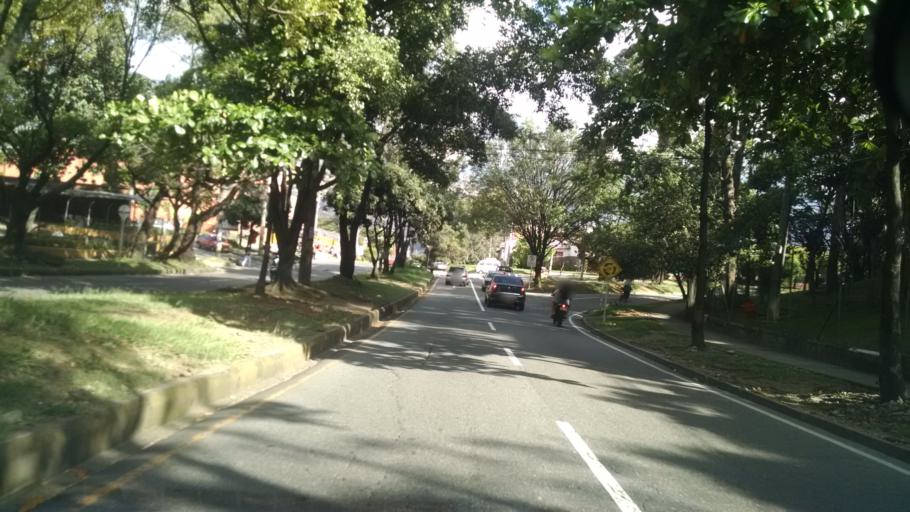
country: CO
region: Antioquia
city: Medellin
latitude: 6.2807
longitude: -75.5796
